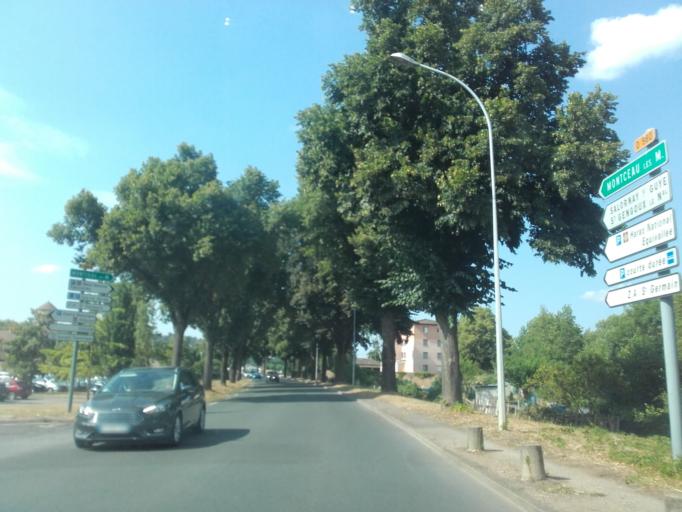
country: FR
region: Bourgogne
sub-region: Departement de Saone-et-Loire
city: Cluny
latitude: 46.4329
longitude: 4.6641
